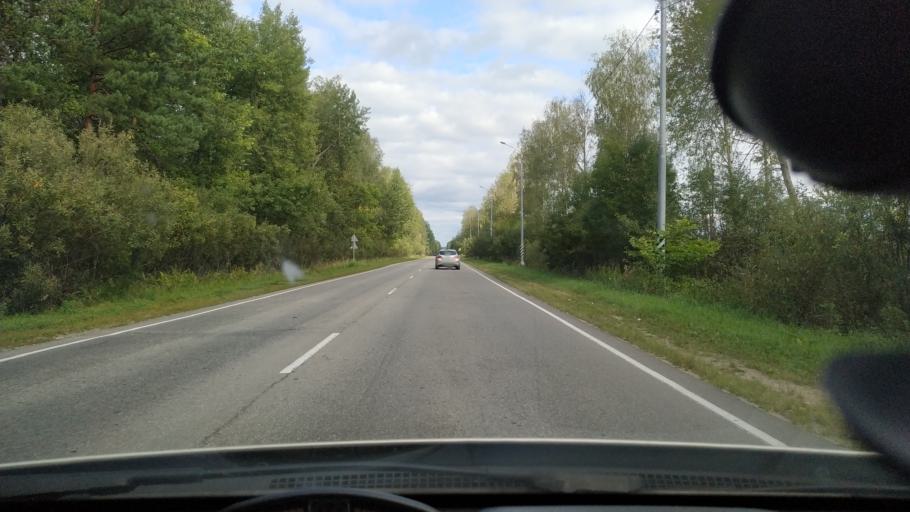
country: RU
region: Moskovskaya
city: Likino-Dulevo
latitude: 55.7291
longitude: 39.0170
